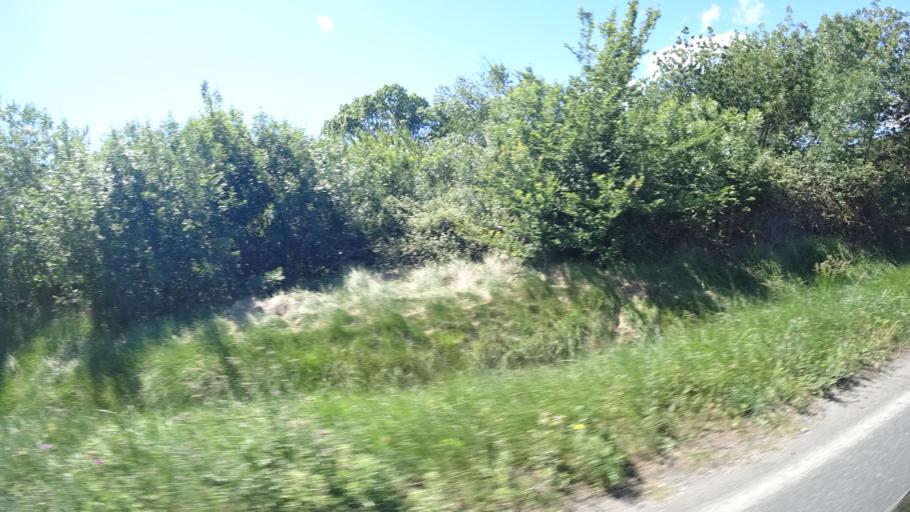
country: FR
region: Languedoc-Roussillon
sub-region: Departement des Pyrenees-Orientales
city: Saint-Nazaire
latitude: 42.6682
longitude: 2.9789
